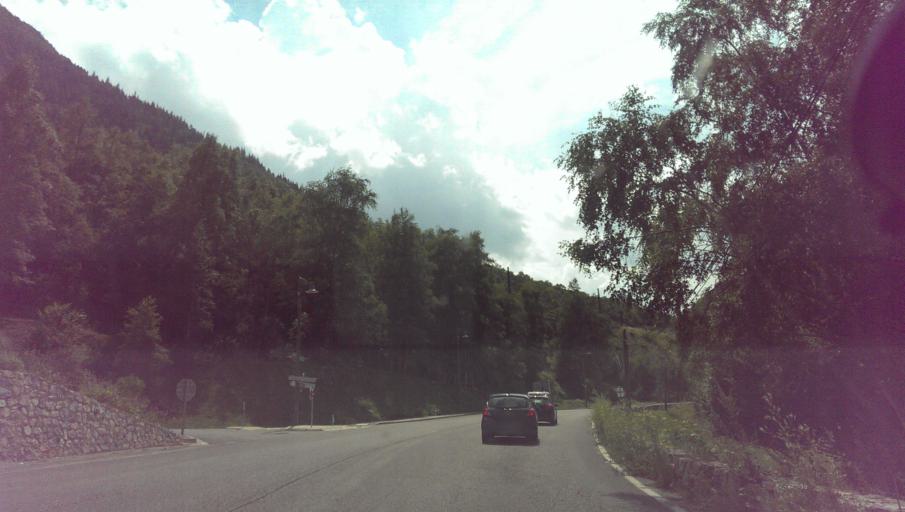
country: AD
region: Encamp
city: Pas de la Casa
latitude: 42.5917
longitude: 1.8035
